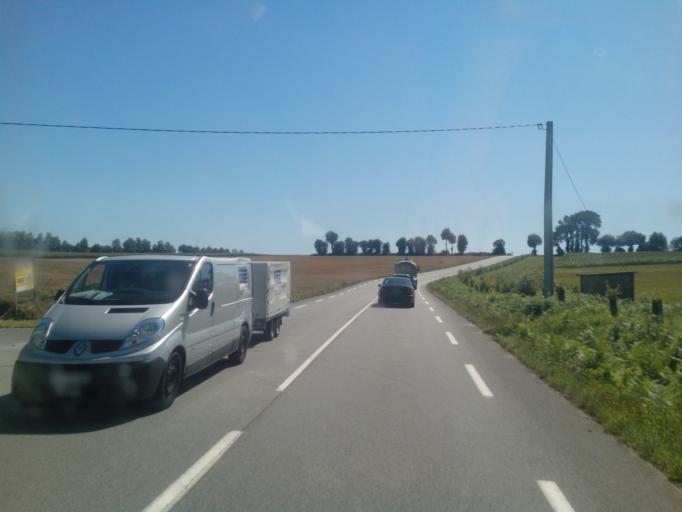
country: FR
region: Brittany
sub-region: Departement du Morbihan
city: Guillac
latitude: 47.8610
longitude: -2.4244
